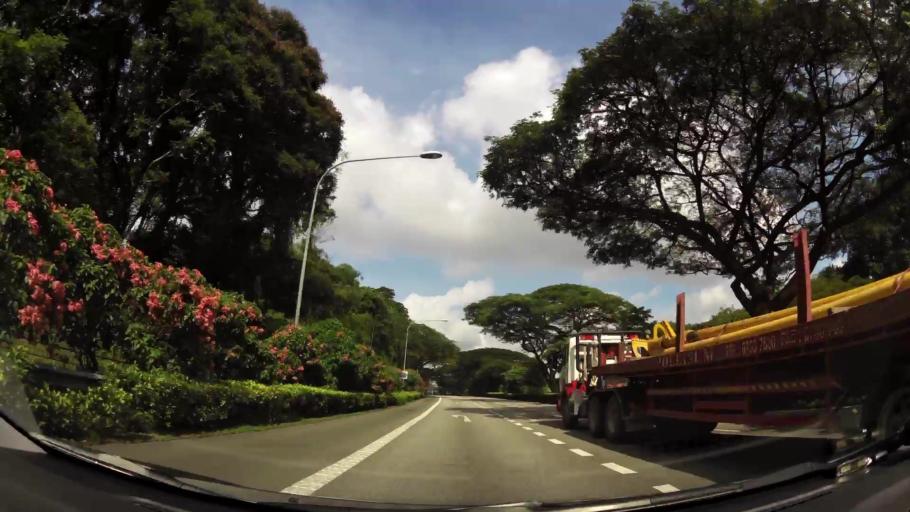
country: SG
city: Singapore
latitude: 1.2763
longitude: 103.8274
